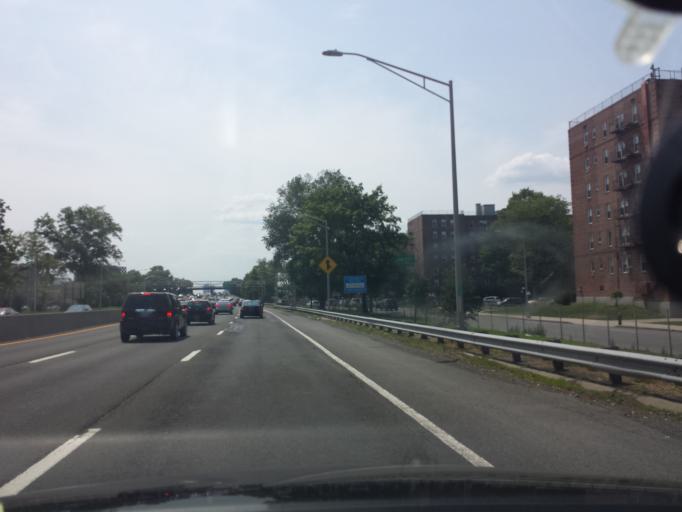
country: US
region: New York
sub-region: Kings County
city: Coney Island
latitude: 40.5837
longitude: -73.9696
